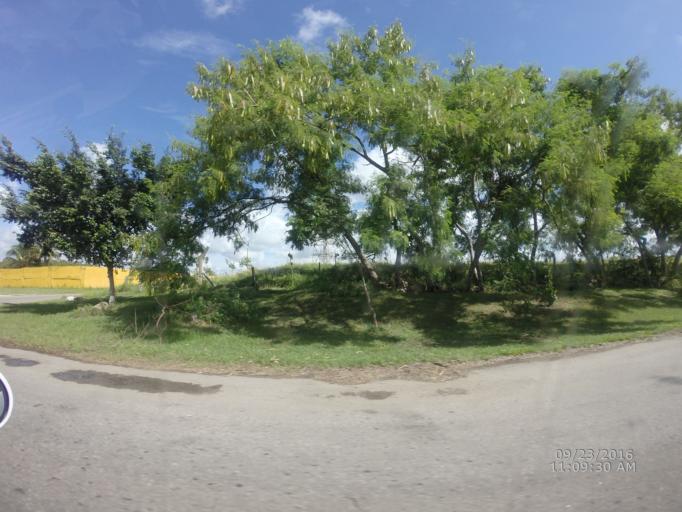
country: CU
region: La Habana
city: Arroyo Naranjo
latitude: 23.0183
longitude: -82.2456
